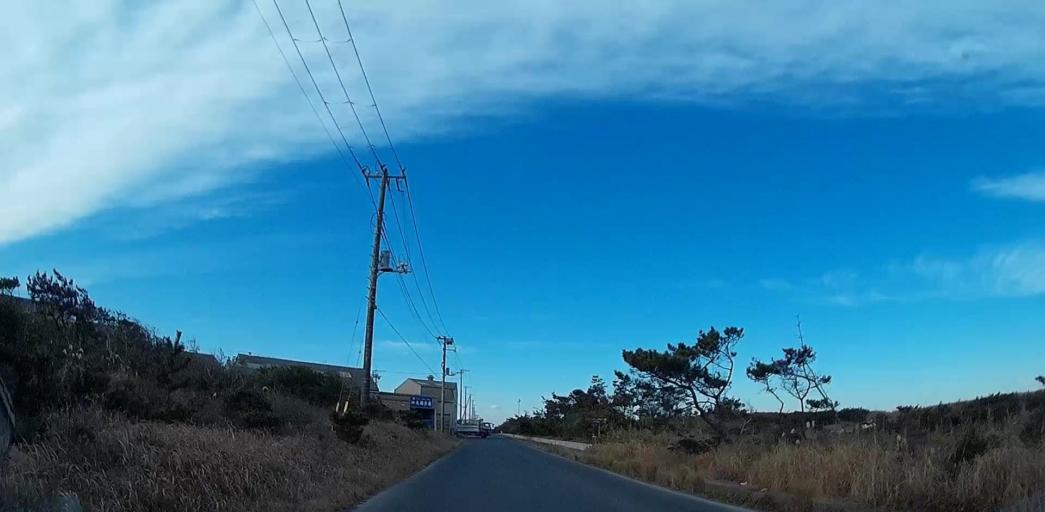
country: JP
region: Chiba
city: Hasaki
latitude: 35.7596
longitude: 140.8237
